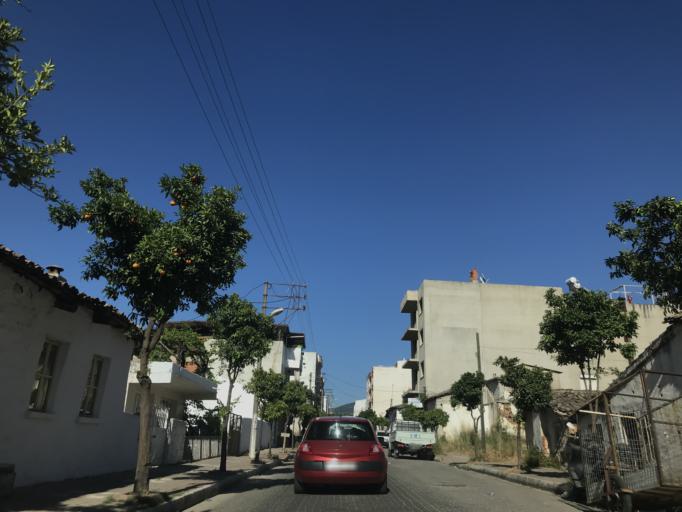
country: TR
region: Aydin
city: Davutlar
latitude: 37.7327
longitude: 27.2878
